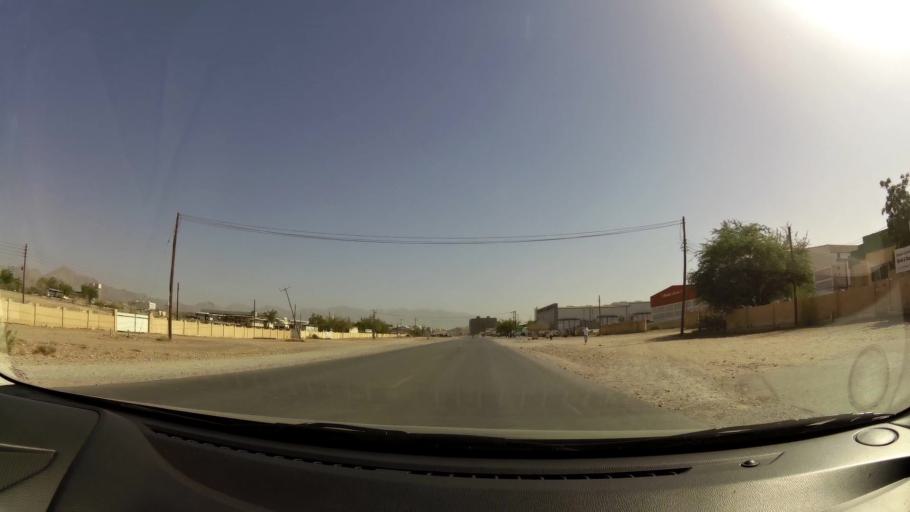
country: OM
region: Muhafazat Masqat
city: Bawshar
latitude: 23.5720
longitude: 58.3510
